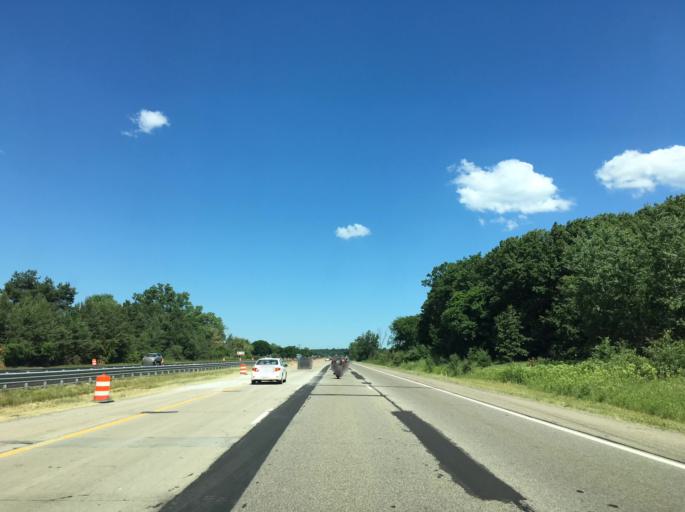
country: US
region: Michigan
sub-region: Oakland County
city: Waterford
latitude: 42.7150
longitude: -83.3408
